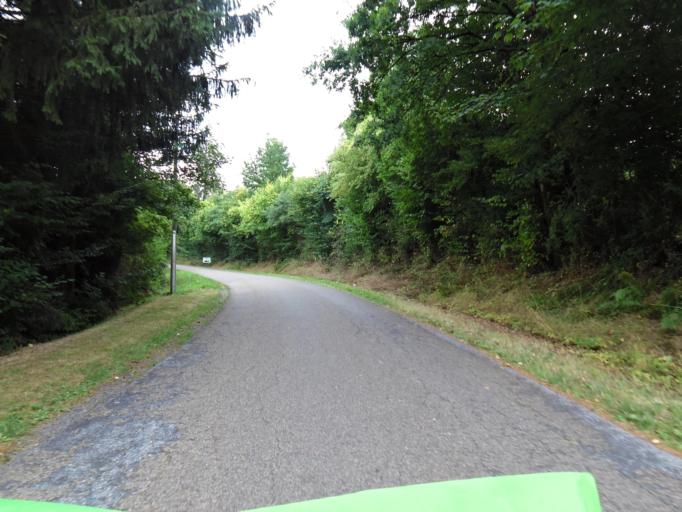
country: BE
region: Wallonia
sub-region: Province de Namur
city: Bievre
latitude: 49.8948
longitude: 5.0069
